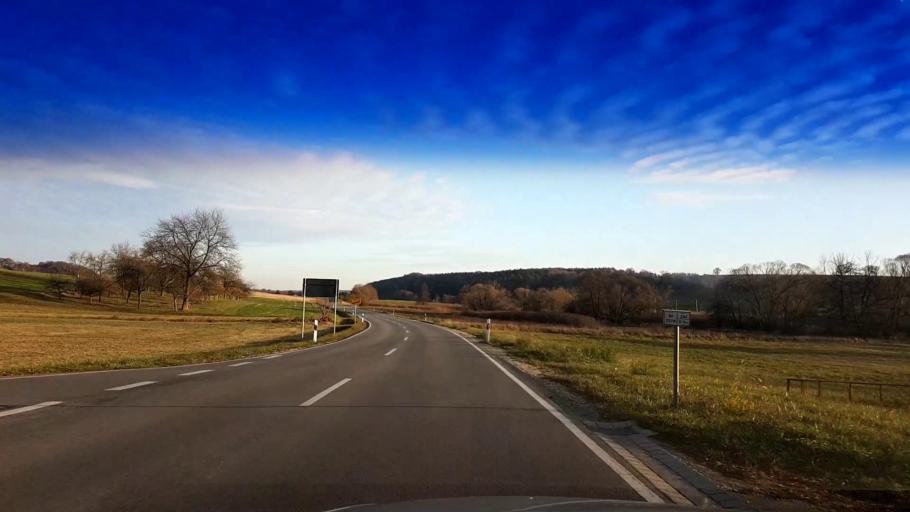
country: DE
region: Bavaria
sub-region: Upper Franconia
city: Priesendorf
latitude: 49.8942
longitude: 10.7302
